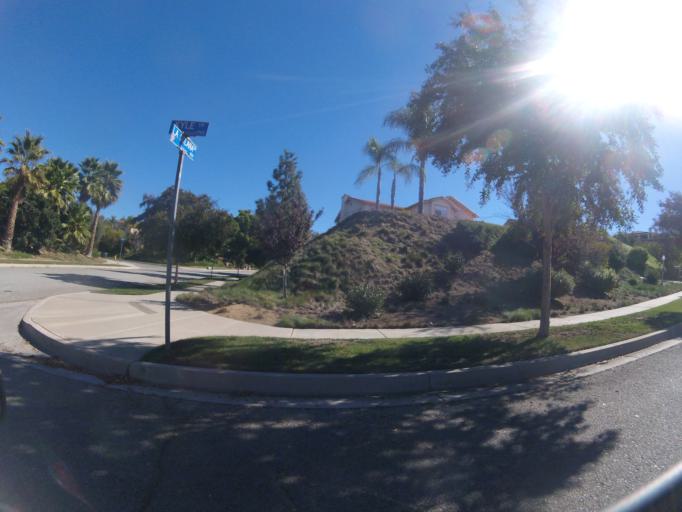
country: US
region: California
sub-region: San Bernardino County
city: Mentone
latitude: 34.0250
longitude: -117.1318
